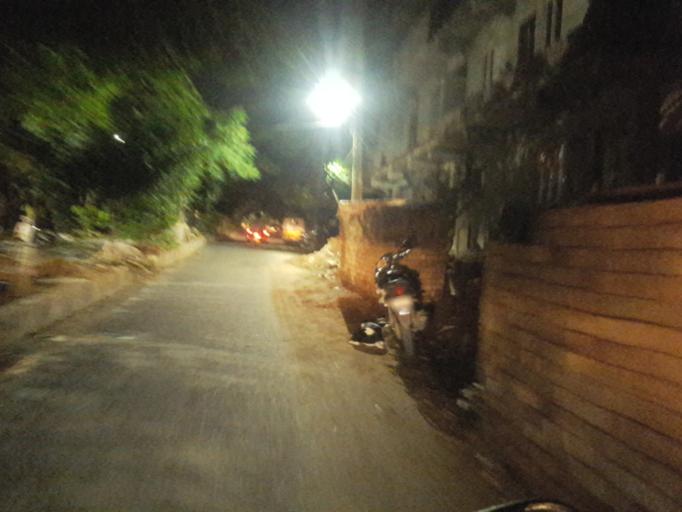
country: IN
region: Telangana
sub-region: Rangareddi
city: Kukatpalli
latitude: 17.4798
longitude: 78.3928
